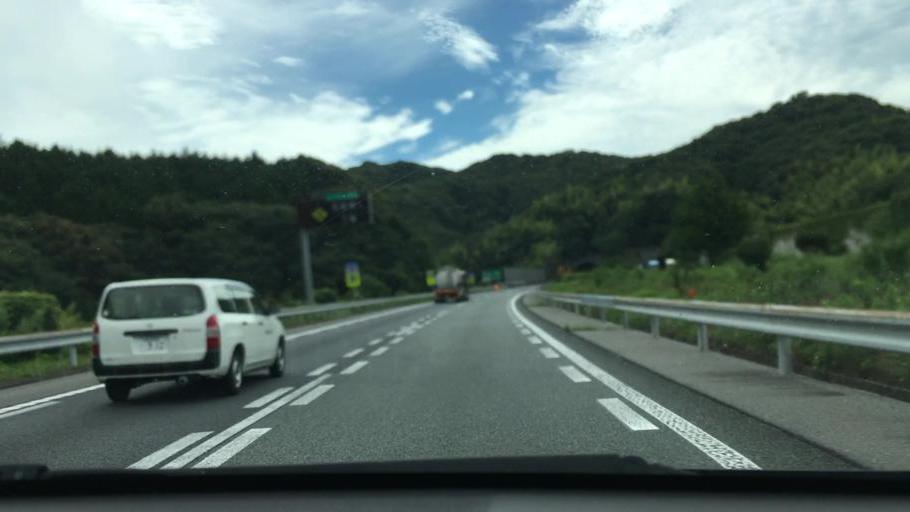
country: JP
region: Yamaguchi
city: Tokuyama
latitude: 34.0661
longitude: 131.6991
